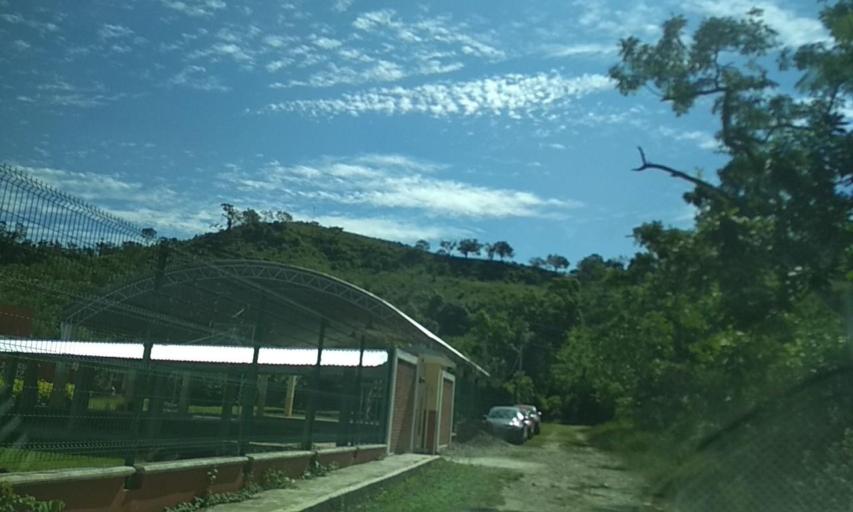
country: MX
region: Veracruz
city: Cazones de Herrera
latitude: 20.6454
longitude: -97.3046
